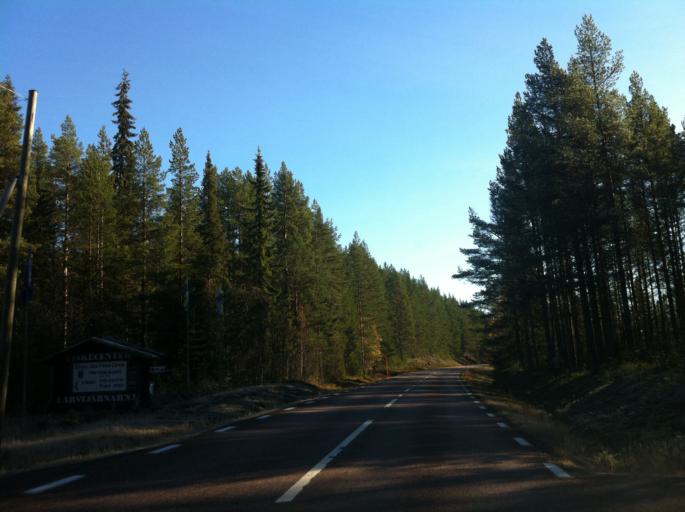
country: NO
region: Hedmark
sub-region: Trysil
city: Innbygda
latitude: 61.8268
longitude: 12.8740
